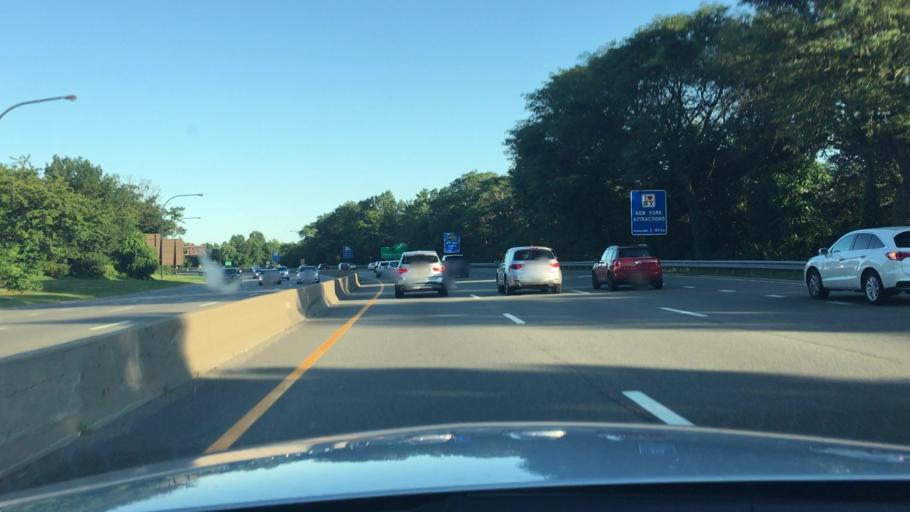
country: US
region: New York
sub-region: Nassau County
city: Carle Place
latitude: 40.7411
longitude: -73.6109
